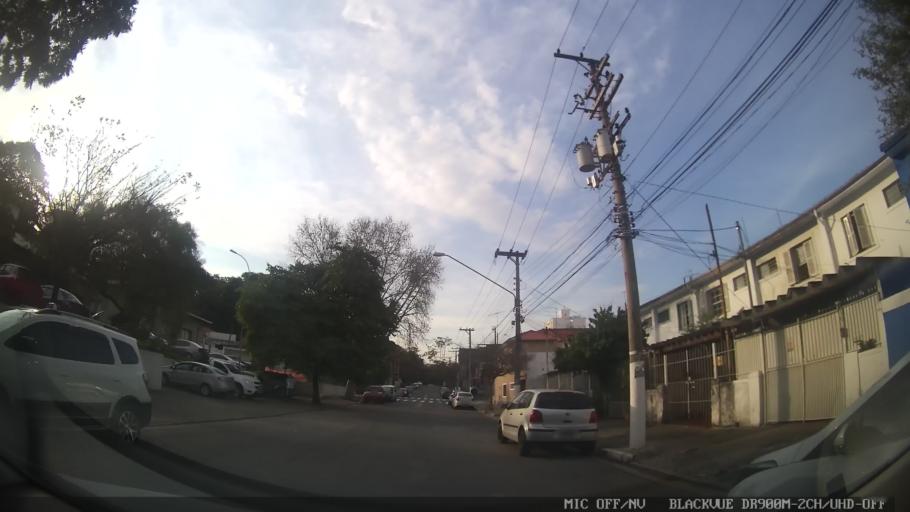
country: BR
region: Sao Paulo
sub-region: Sao Paulo
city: Sao Paulo
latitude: -23.5874
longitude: -46.6084
